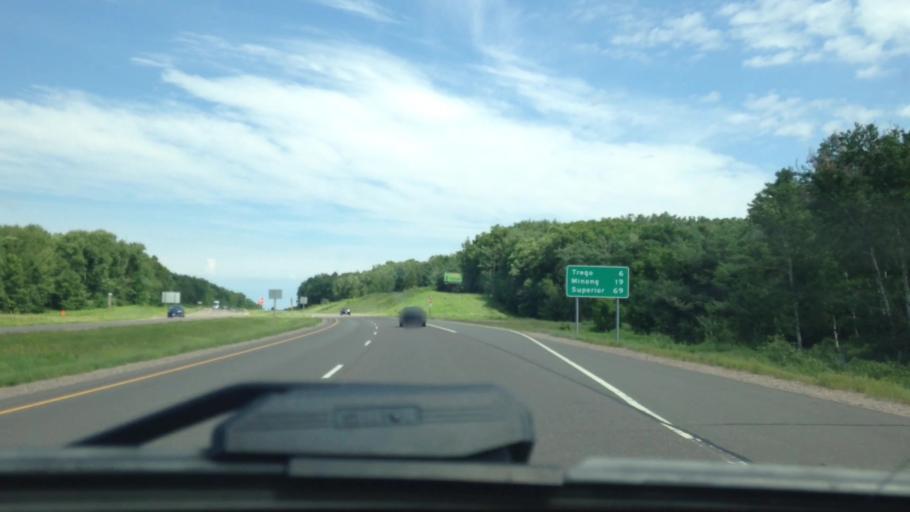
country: US
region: Wisconsin
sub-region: Washburn County
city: Spooner
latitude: 45.8275
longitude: -91.8560
